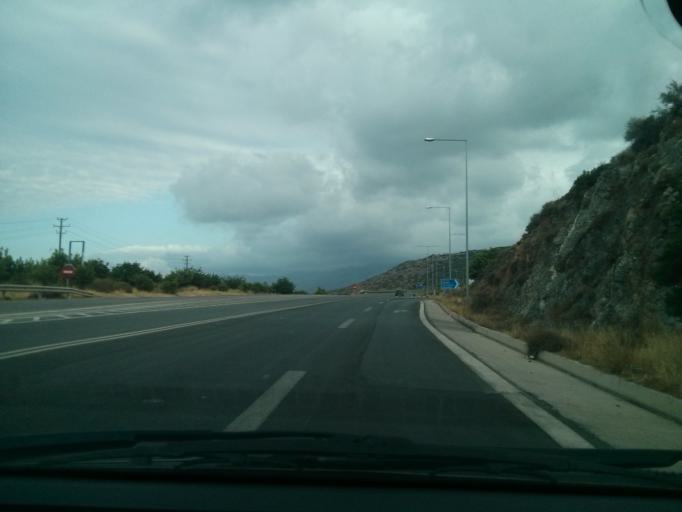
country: GR
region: Crete
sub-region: Nomos Irakleiou
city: Limin Khersonisou
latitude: 35.3012
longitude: 25.3977
